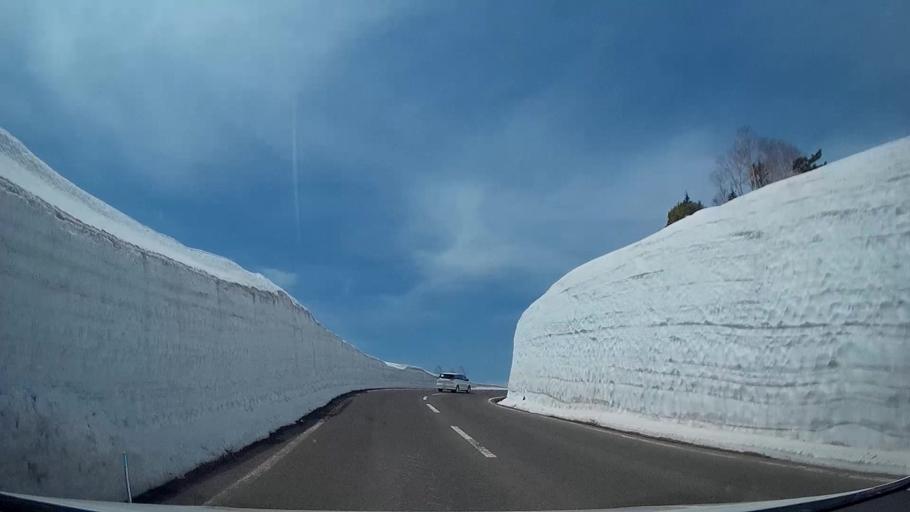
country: JP
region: Akita
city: Hanawa
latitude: 39.9512
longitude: 140.8632
